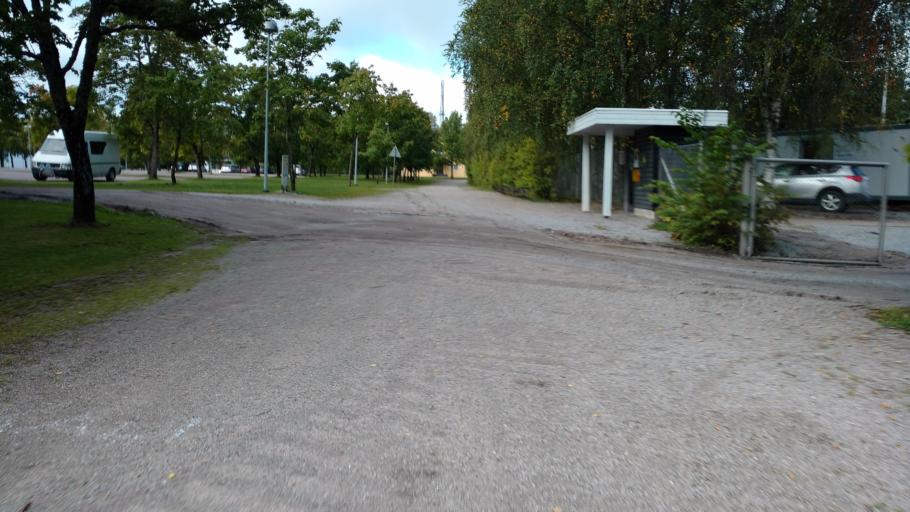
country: FI
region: Varsinais-Suomi
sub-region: Salo
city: Salo
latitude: 60.3802
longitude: 23.1388
